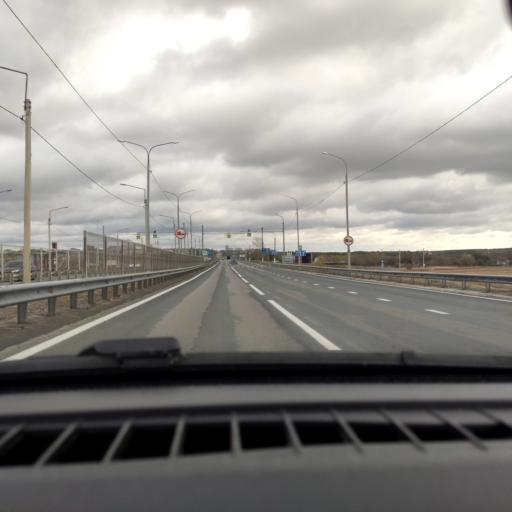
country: RU
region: Voronezj
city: Pridonskoy
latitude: 51.6508
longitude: 39.0617
